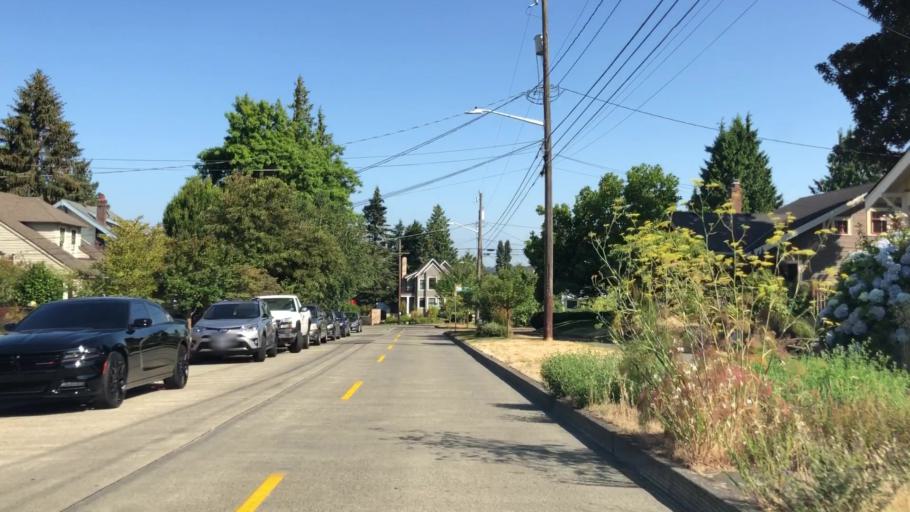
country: US
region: Washington
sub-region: King County
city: Seattle
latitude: 47.6710
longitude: -122.3330
